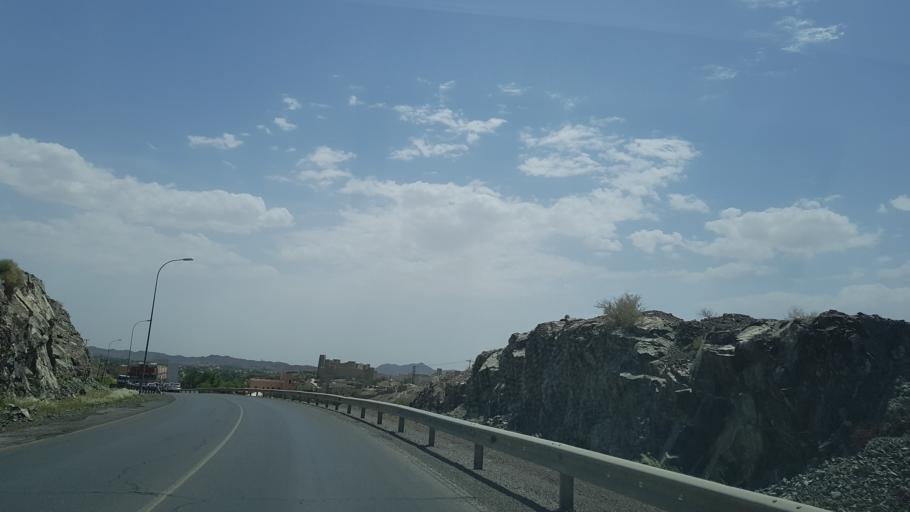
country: OM
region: Muhafazat ad Dakhiliyah
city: Bahla'
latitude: 22.9710
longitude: 57.3021
